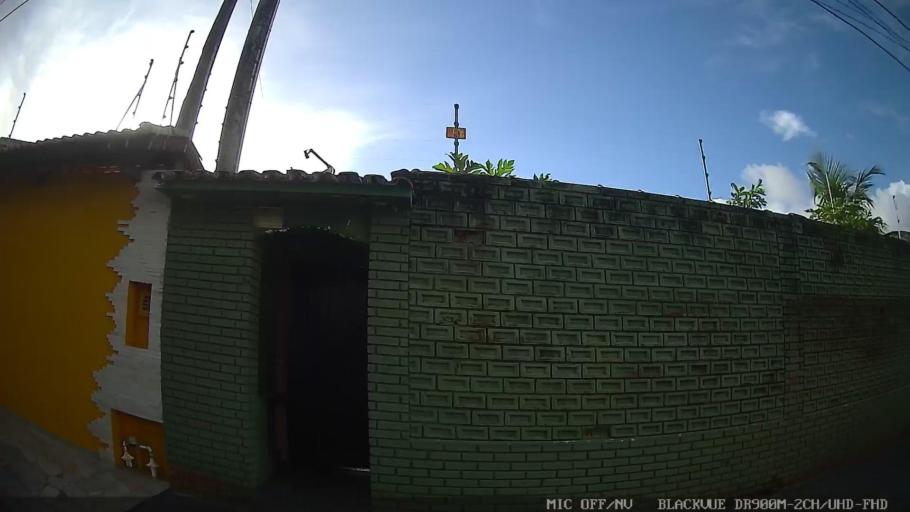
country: BR
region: Sao Paulo
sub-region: Itanhaem
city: Itanhaem
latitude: -24.2104
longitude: -46.8407
